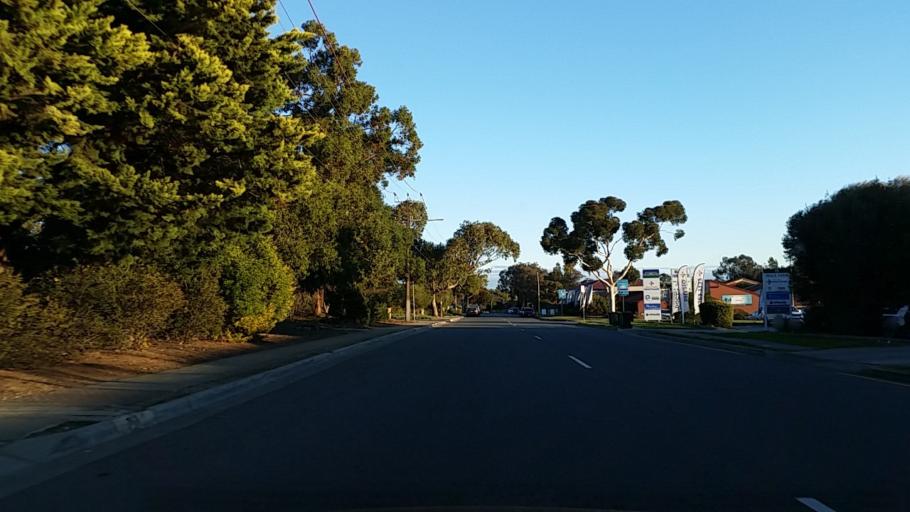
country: AU
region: South Australia
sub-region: Salisbury
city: Ingle Farm
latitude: -34.8298
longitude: 138.6510
